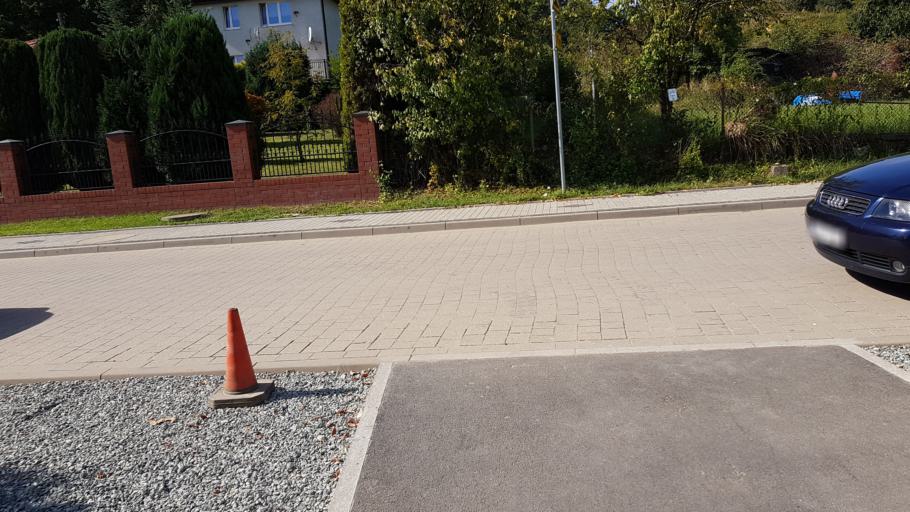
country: PL
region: West Pomeranian Voivodeship
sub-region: Powiat policki
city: Przeclaw
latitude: 53.3462
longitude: 14.4975
